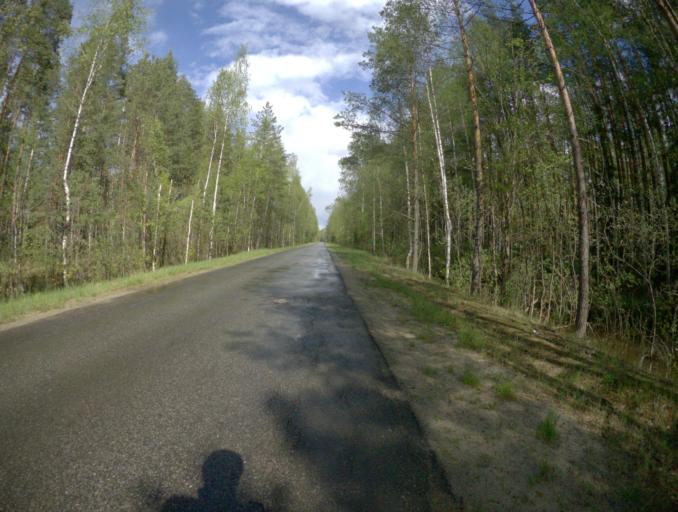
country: RU
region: Vladimir
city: Urshel'skiy
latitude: 55.5831
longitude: 40.2000
